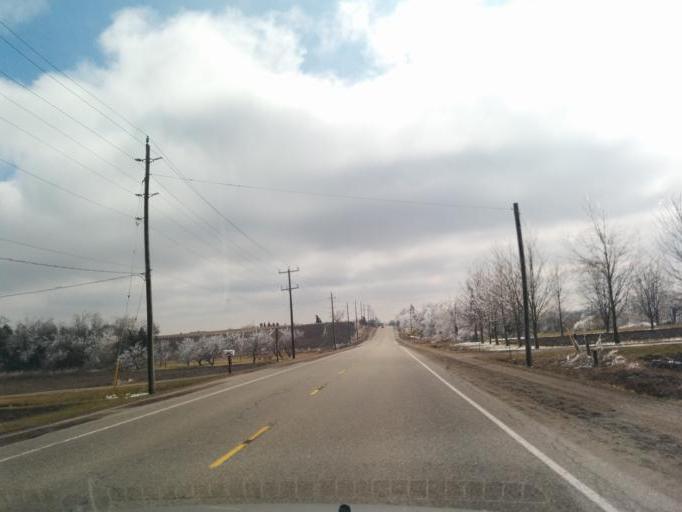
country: CA
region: Ontario
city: Waterloo
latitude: 43.6385
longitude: -80.5489
